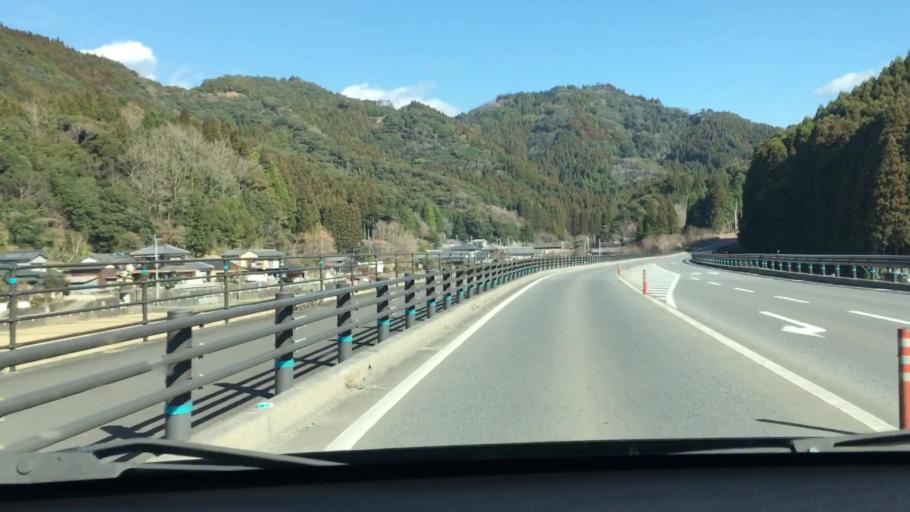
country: JP
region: Oita
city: Saiki
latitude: 32.9581
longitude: 131.8460
